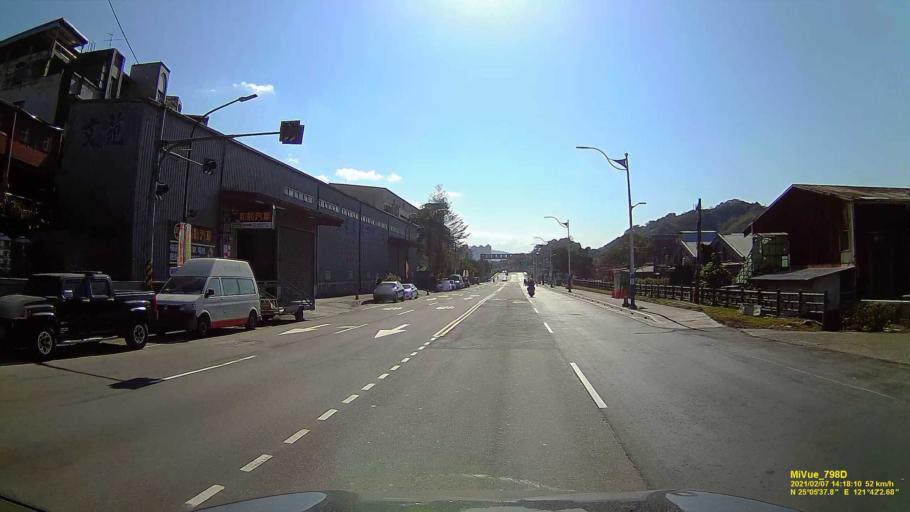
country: TW
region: Taiwan
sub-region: Keelung
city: Keelung
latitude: 25.0927
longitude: 121.6995
